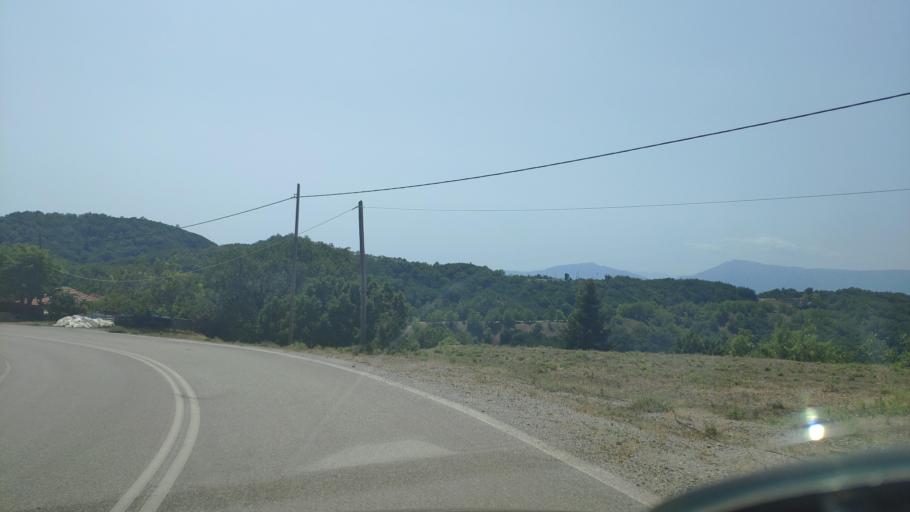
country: GR
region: Epirus
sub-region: Nomos Artas
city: Ano Kalentini
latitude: 39.2408
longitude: 21.2052
